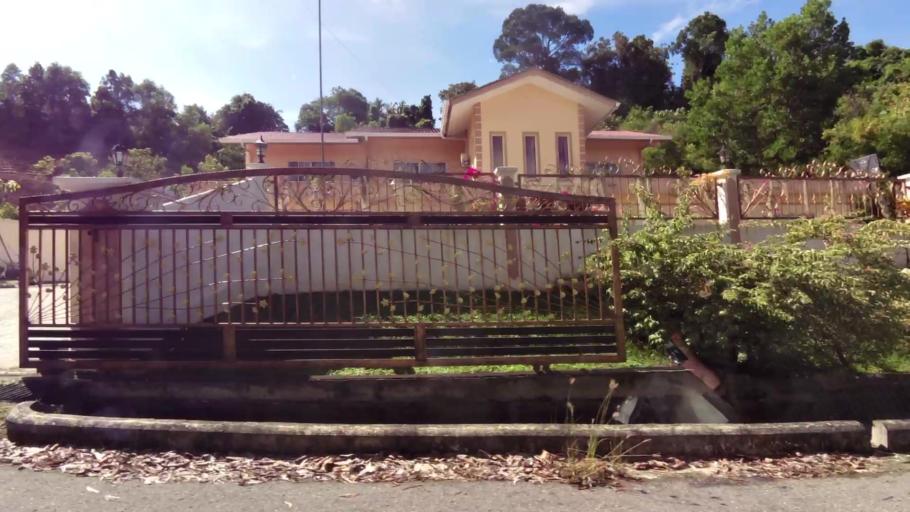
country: BN
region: Brunei and Muara
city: Bandar Seri Begawan
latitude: 4.9584
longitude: 114.9476
